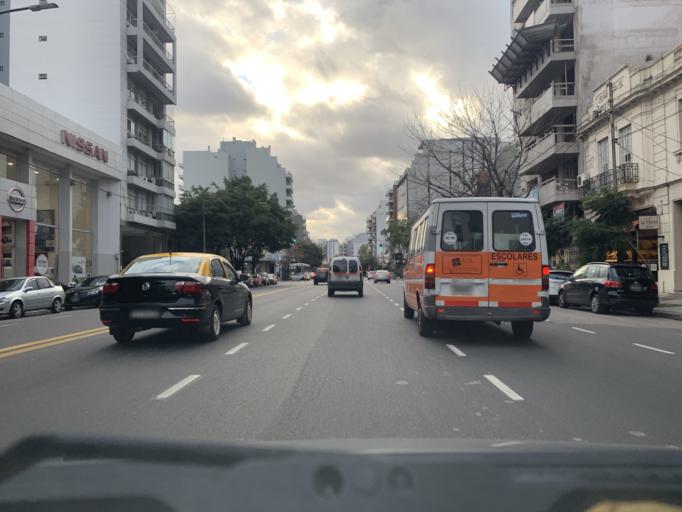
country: AR
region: Buenos Aires F.D.
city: Colegiales
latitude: -34.5795
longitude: -58.4540
